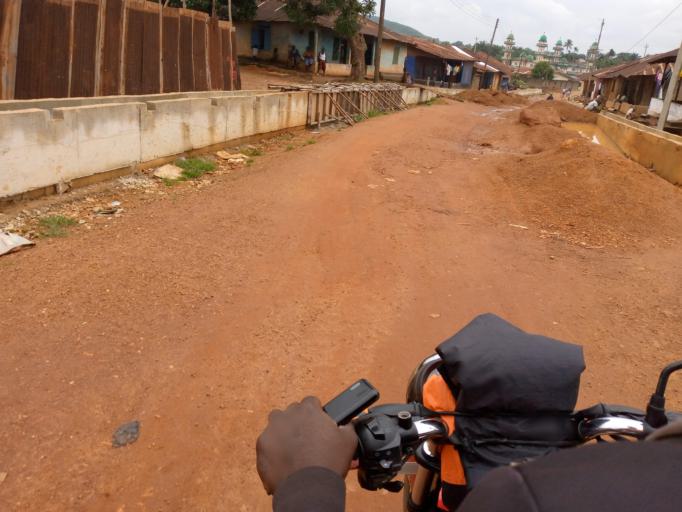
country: SL
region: Eastern Province
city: Kenema
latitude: 7.8711
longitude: -11.1890
